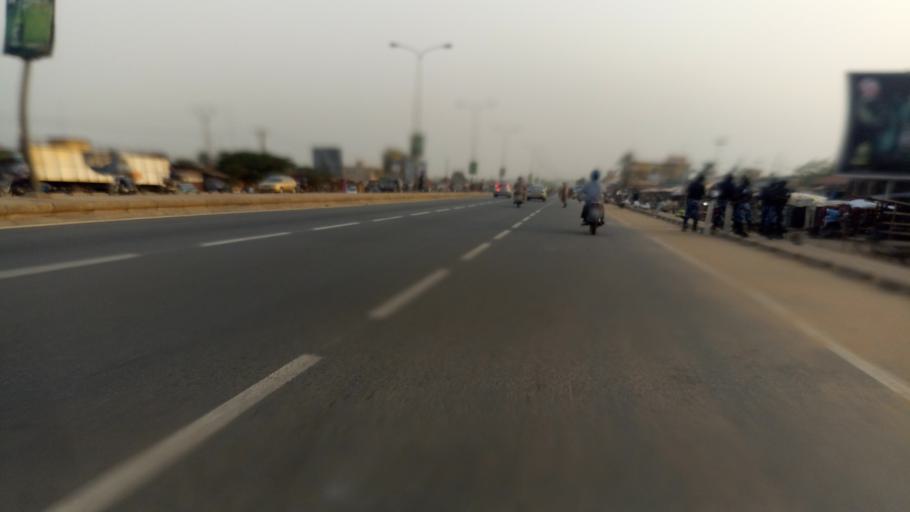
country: TG
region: Maritime
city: Lome
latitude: 6.2548
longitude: 1.2085
